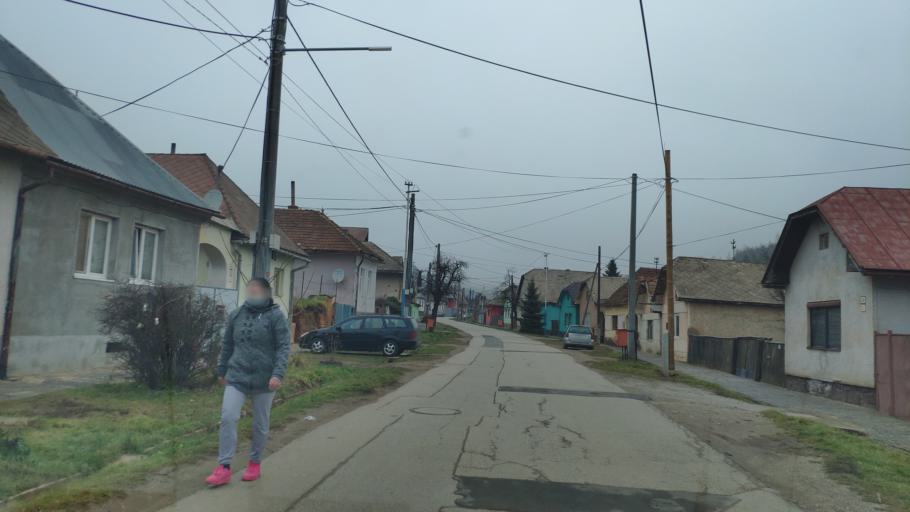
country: SK
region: Banskobystricky
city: Revuca
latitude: 48.6338
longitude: 20.2373
